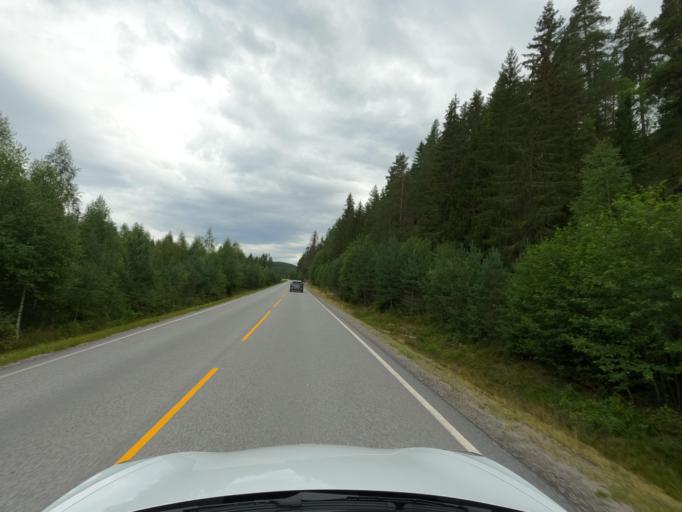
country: NO
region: Telemark
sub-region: Hjartdal
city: Sauland
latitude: 59.7074
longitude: 9.0122
